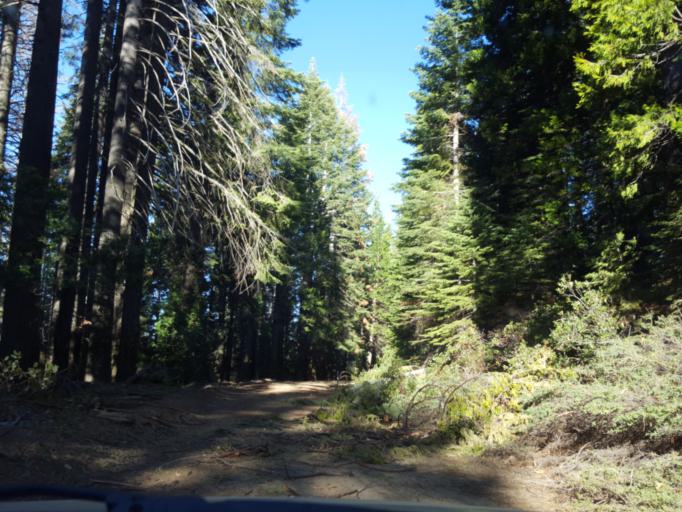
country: US
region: California
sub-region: Madera County
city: Oakhurst
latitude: 37.3756
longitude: -119.4993
